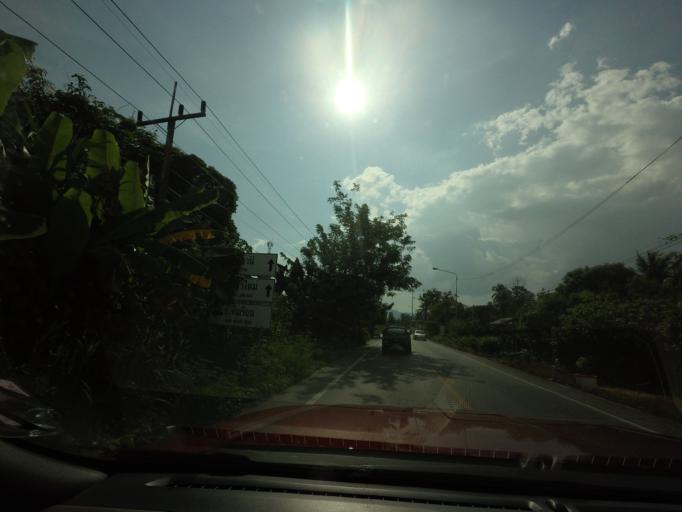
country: TH
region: Yala
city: Yala
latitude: 6.5586
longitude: 101.2208
